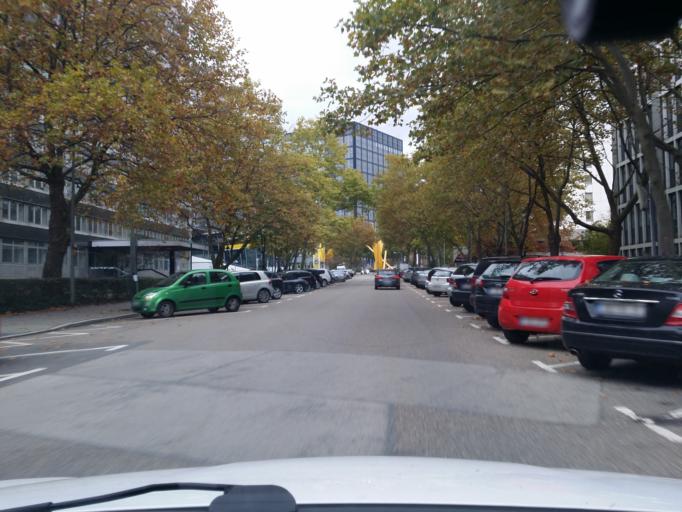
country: DE
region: Hesse
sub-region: Regierungsbezirk Darmstadt
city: Eschborn
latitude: 50.1339
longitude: 8.5743
